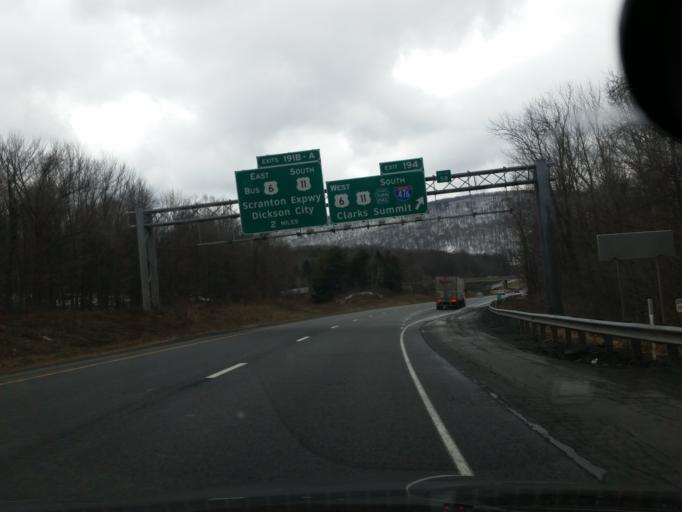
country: US
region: Pennsylvania
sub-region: Lackawanna County
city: Chinchilla
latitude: 41.4860
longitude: -75.6786
